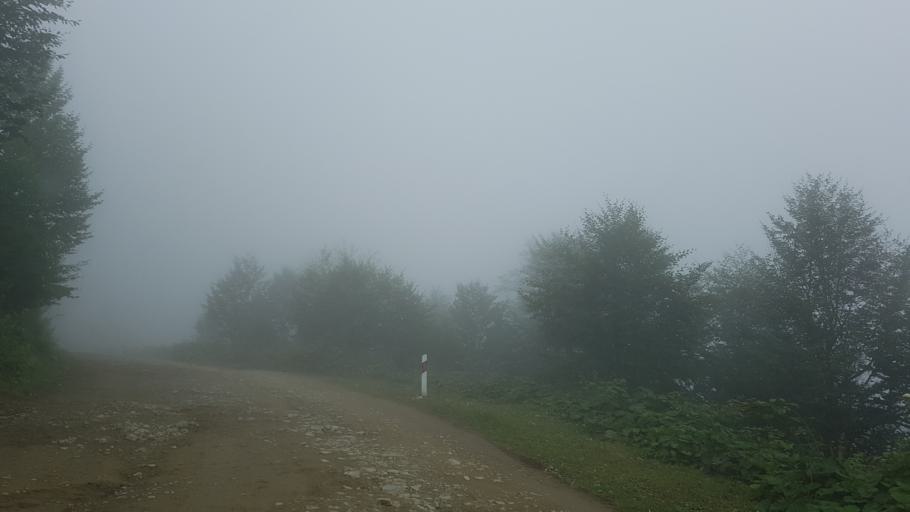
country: GE
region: Guria
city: Ozurgeti
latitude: 41.8394
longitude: 42.1440
